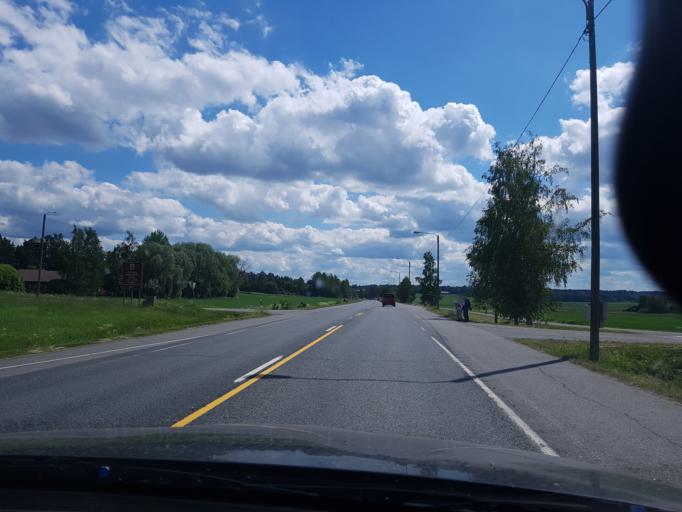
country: FI
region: Haeme
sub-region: Haemeenlinna
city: Parola
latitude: 61.0525
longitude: 24.3940
